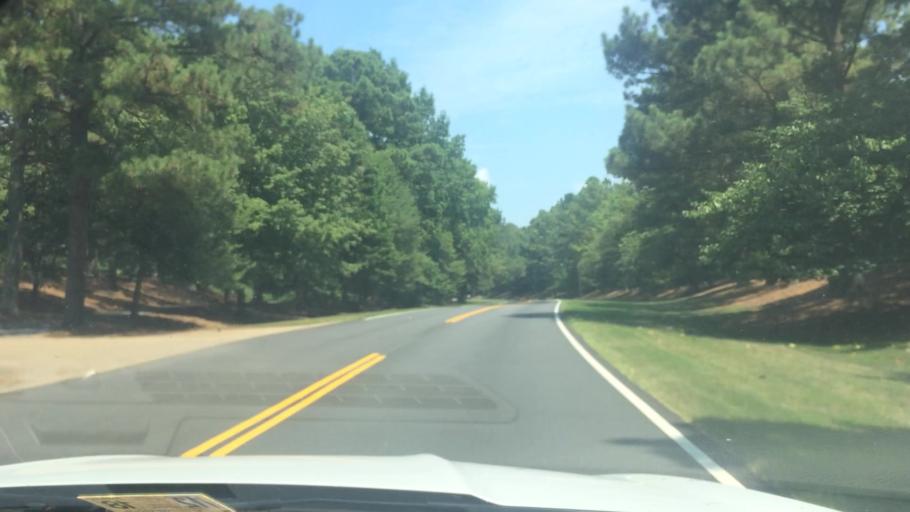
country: US
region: Virginia
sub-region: City of Williamsburg
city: Williamsburg
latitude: 37.2323
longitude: -76.6558
